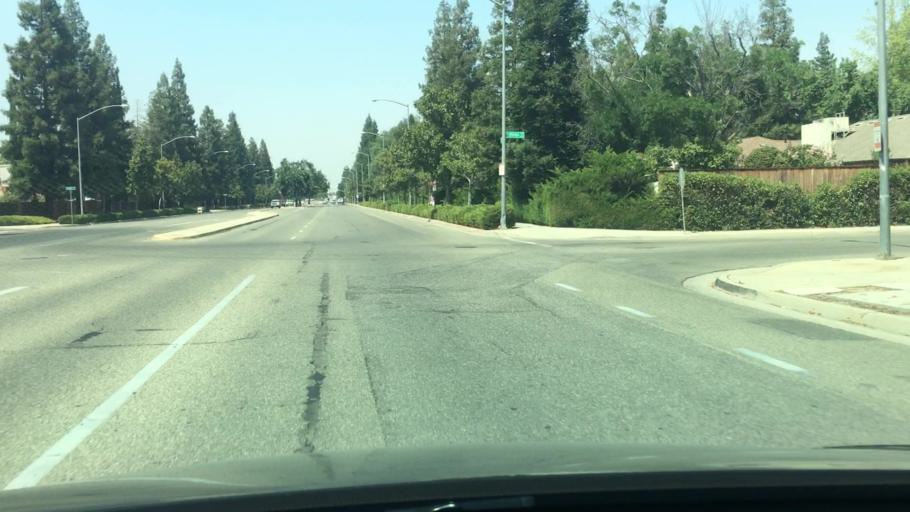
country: US
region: California
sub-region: Fresno County
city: Clovis
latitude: 36.8555
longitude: -119.7567
